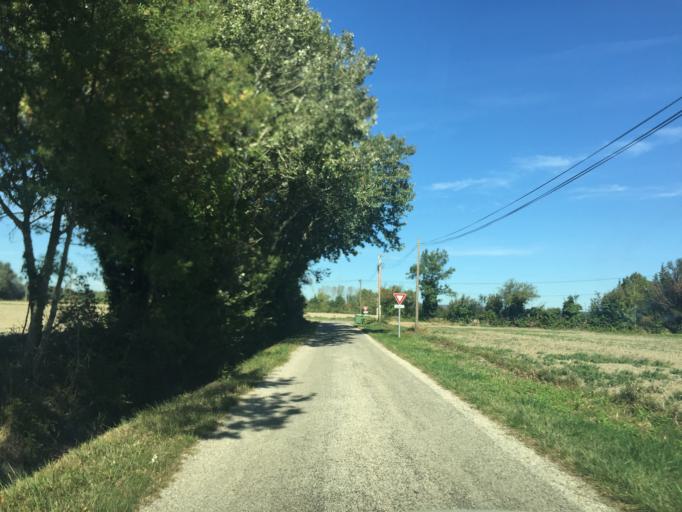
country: FR
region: Provence-Alpes-Cote d'Azur
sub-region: Departement du Vaucluse
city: Caderousse
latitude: 44.1374
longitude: 4.7404
